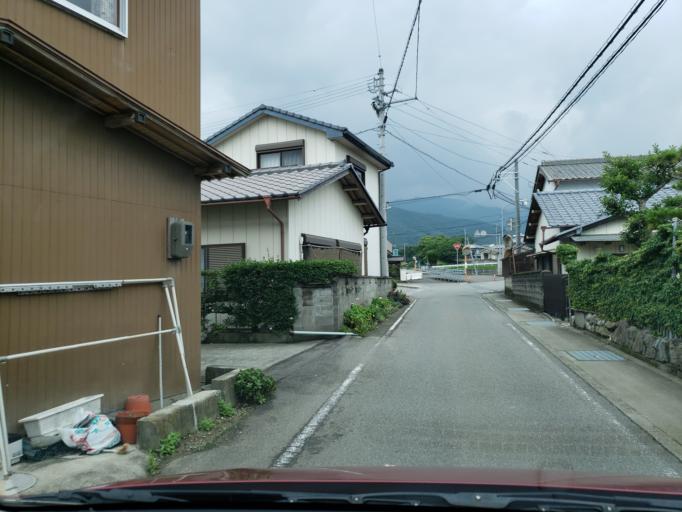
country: JP
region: Tokushima
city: Wakimachi
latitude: 34.0958
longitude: 134.2279
